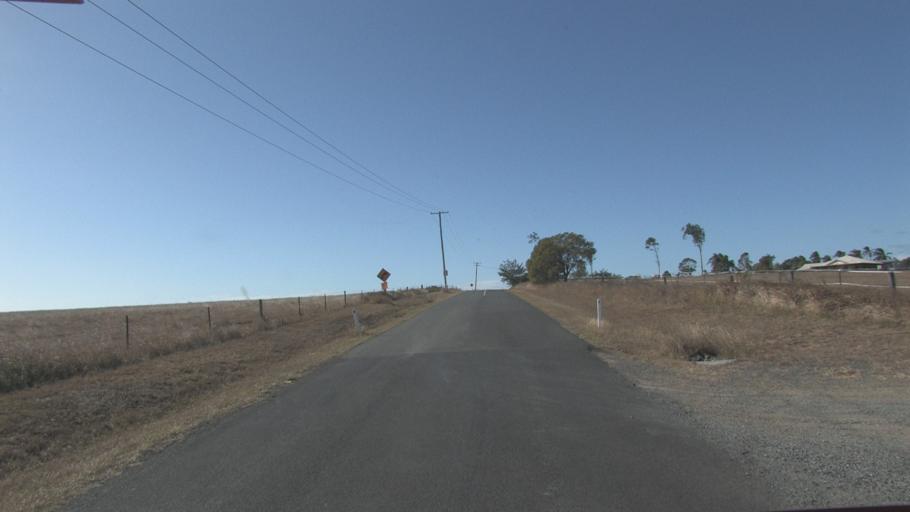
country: AU
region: Queensland
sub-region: Logan
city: Cedar Vale
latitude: -27.8542
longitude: 152.9687
